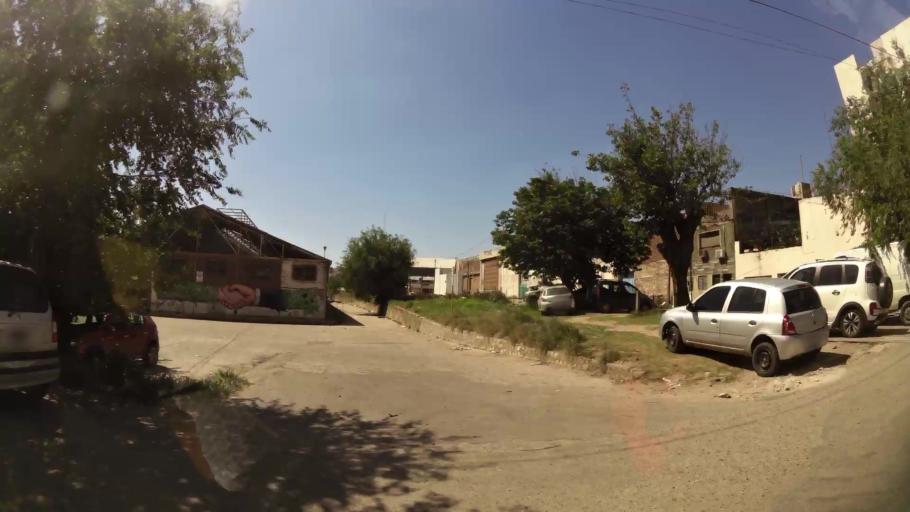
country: AR
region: Cordoba
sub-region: Departamento de Capital
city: Cordoba
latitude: -31.4079
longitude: -64.1742
